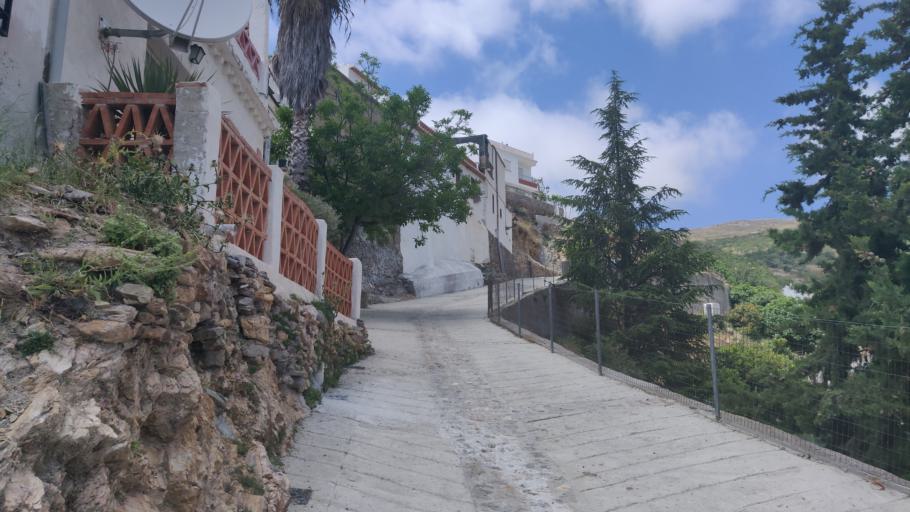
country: ES
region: Andalusia
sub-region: Provincia de Granada
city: Rubite
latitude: 36.8079
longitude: -3.3481
